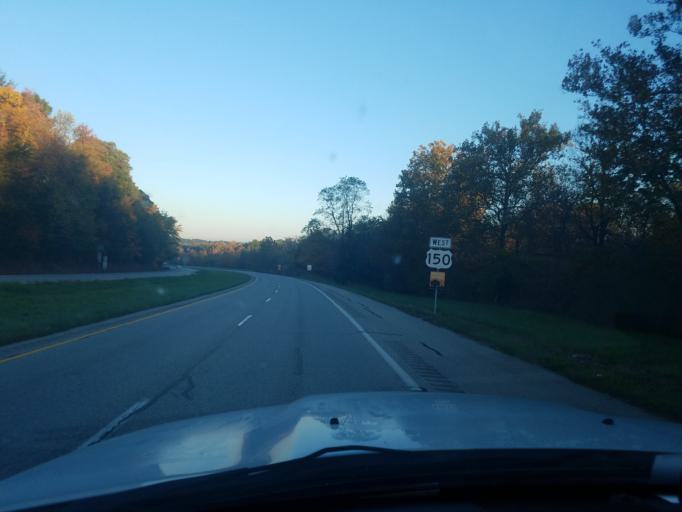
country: US
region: Indiana
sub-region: Floyd County
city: Galena
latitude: 38.3357
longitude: -85.8997
